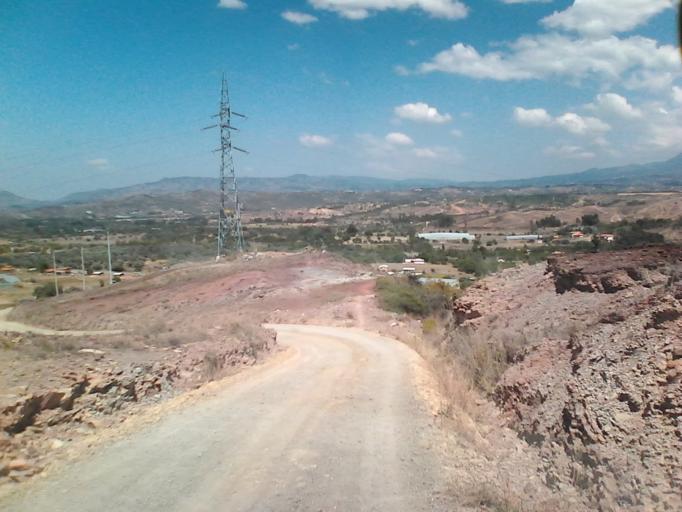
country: CO
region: Boyaca
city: Sachica
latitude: 5.6015
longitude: -73.5620
